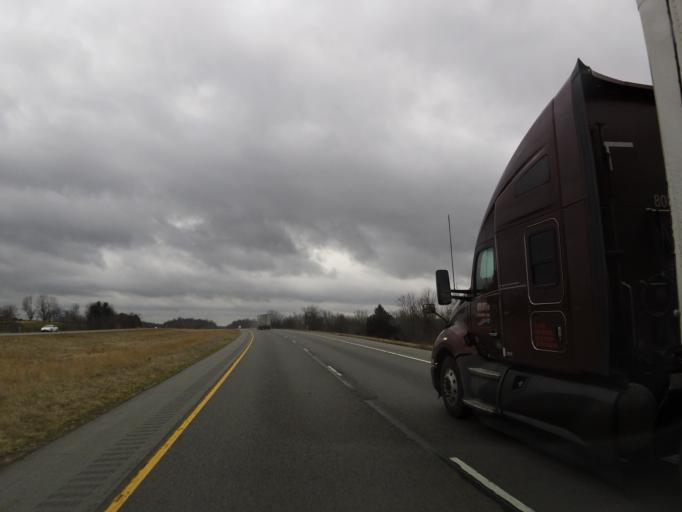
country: US
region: Illinois
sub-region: Massac County
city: Metropolis
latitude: 37.2705
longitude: -88.7420
